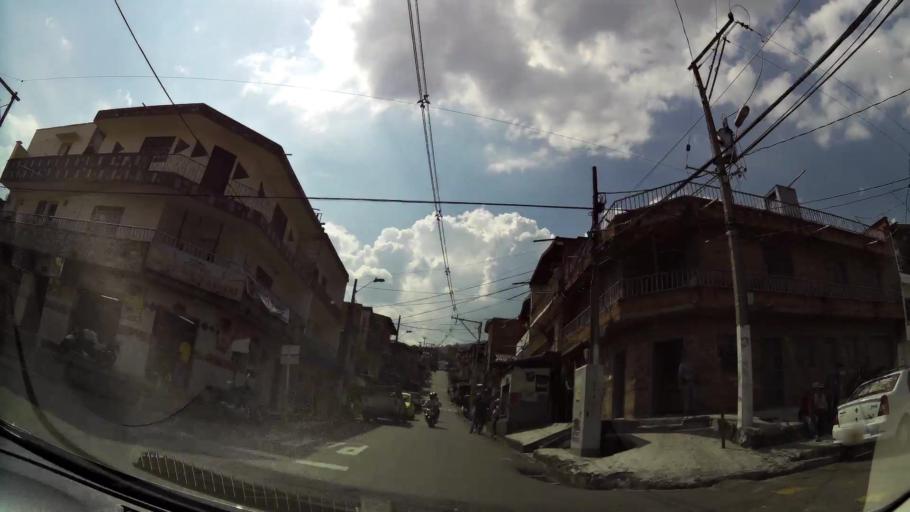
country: CO
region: Antioquia
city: Medellin
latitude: 6.2884
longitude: -75.5790
